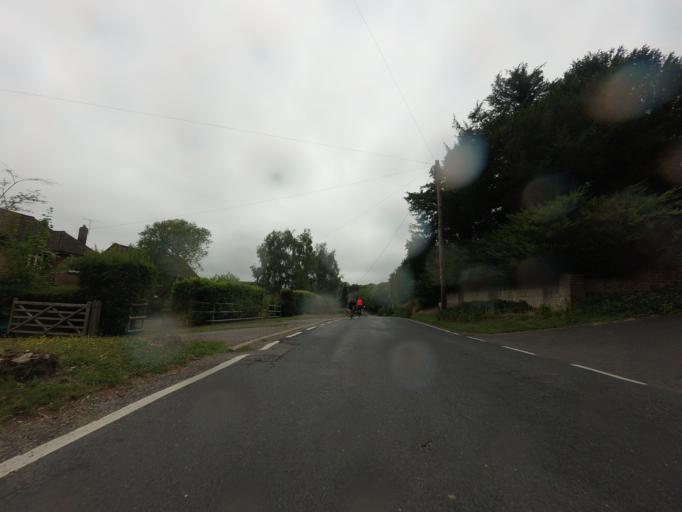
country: GB
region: England
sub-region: Kent
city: Kemsing
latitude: 51.3101
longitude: 0.2164
